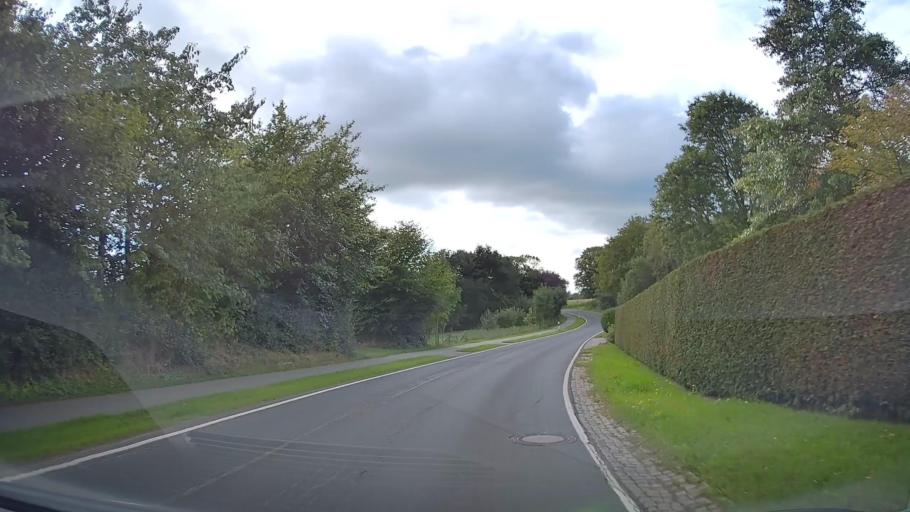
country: DE
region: Schleswig-Holstein
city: Niesgrau
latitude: 54.7631
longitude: 9.8030
